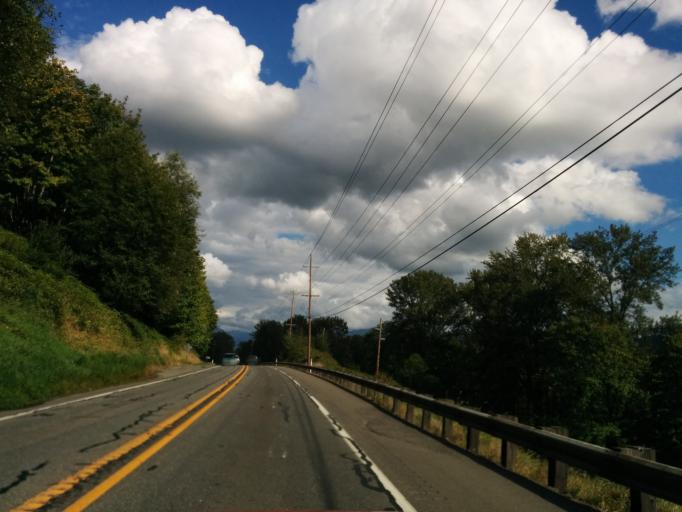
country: US
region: Washington
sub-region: Snohomish County
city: Monroe
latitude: 47.8565
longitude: -121.9570
